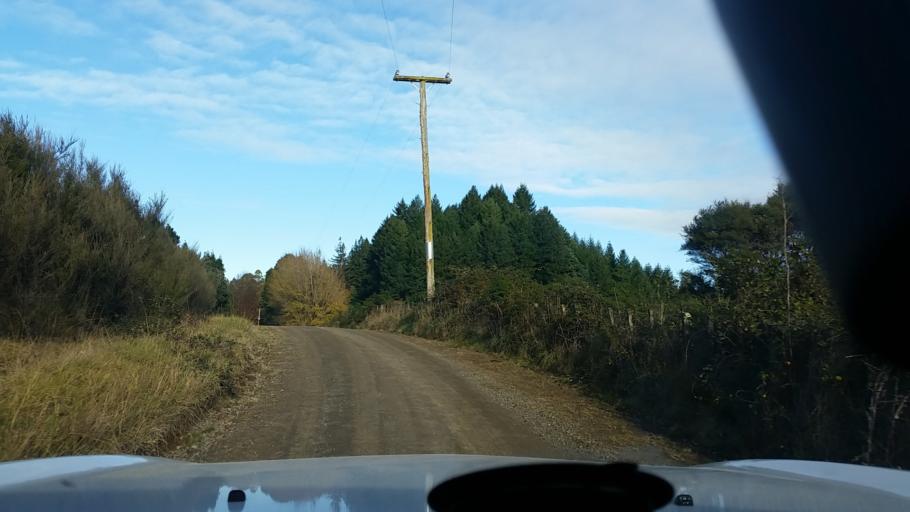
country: NZ
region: Hawke's Bay
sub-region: Napier City
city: Napier
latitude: -39.2411
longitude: 176.8102
